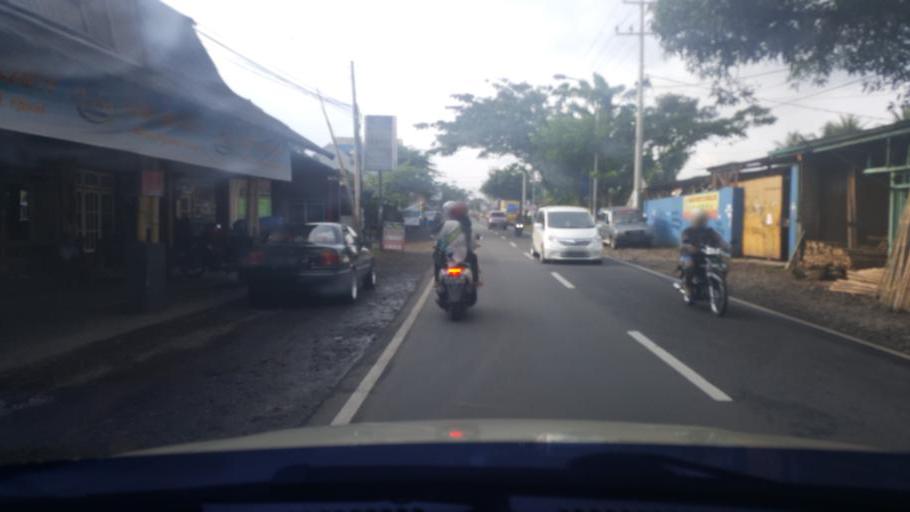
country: ID
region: West Java
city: Jati
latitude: -7.3003
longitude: 108.2023
